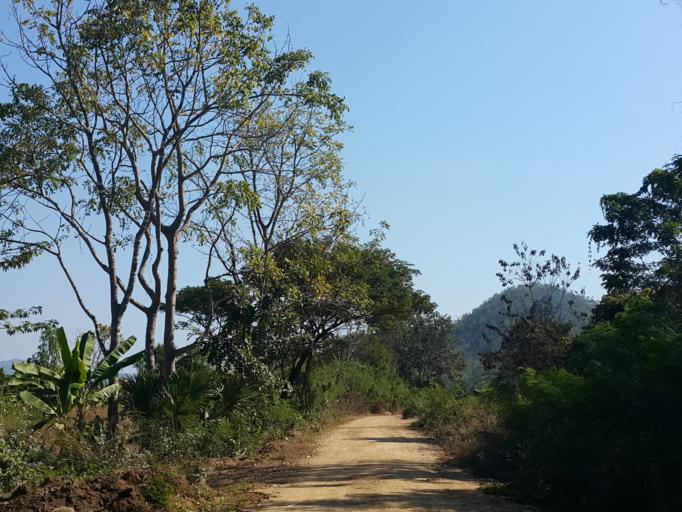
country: TH
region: Sukhothai
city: Thung Saliam
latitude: 17.3152
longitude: 99.4425
